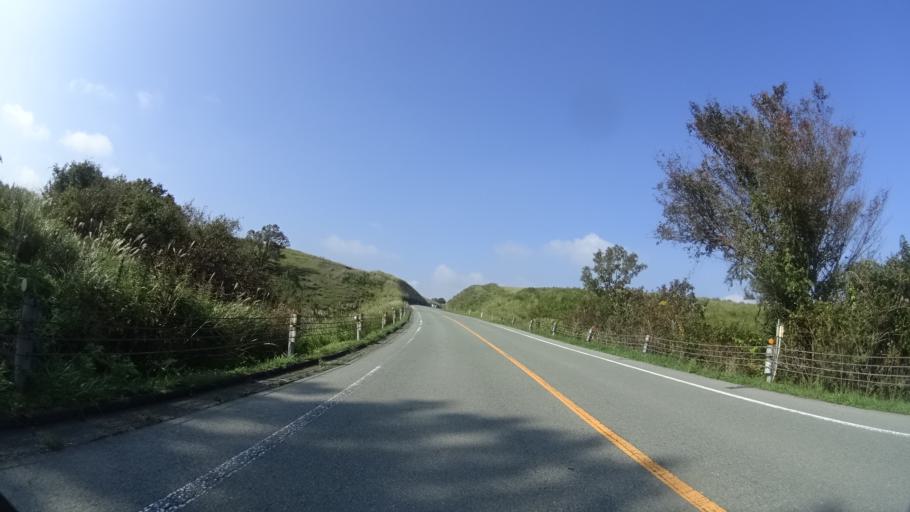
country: JP
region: Kumamoto
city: Aso
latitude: 33.0162
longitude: 131.0688
